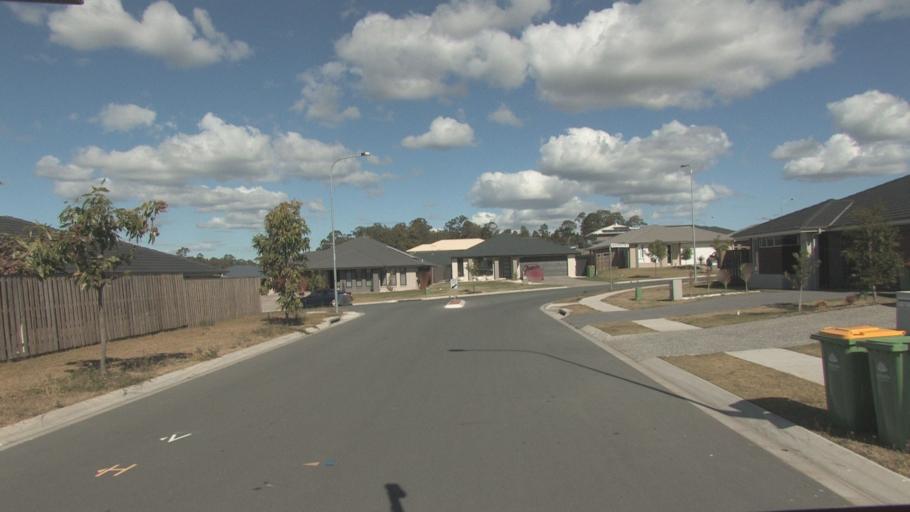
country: AU
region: Queensland
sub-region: Logan
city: Logan Reserve
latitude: -27.7137
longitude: 153.0846
